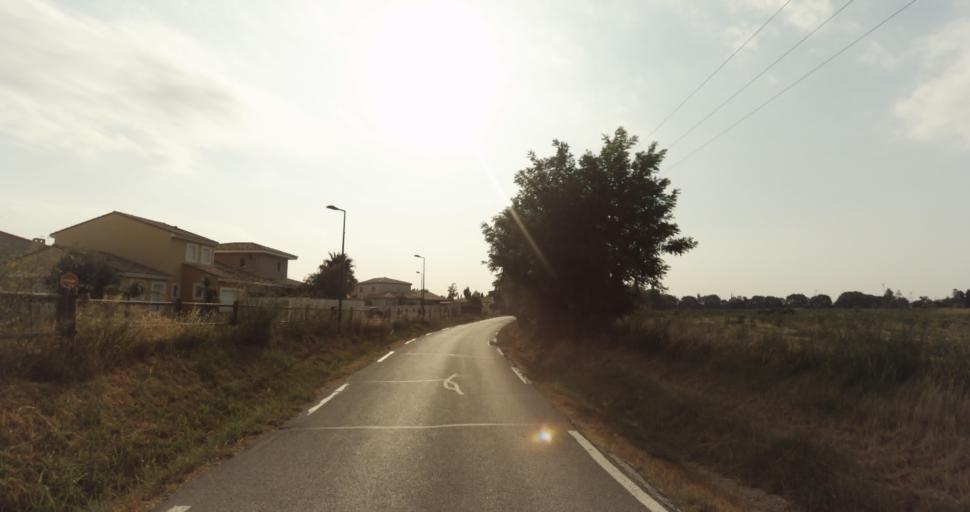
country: FR
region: Languedoc-Roussillon
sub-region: Departement des Pyrenees-Orientales
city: Corneilla-del-Vercol
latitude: 42.6242
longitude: 2.9556
